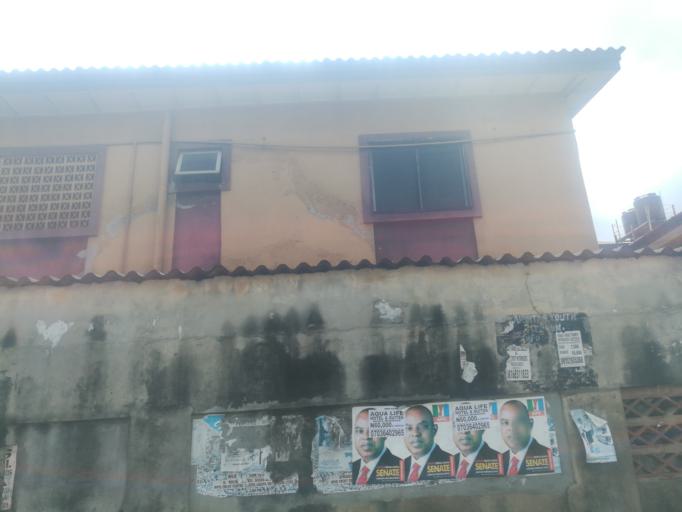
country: NG
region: Lagos
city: Ojota
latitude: 6.5971
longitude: 3.3902
